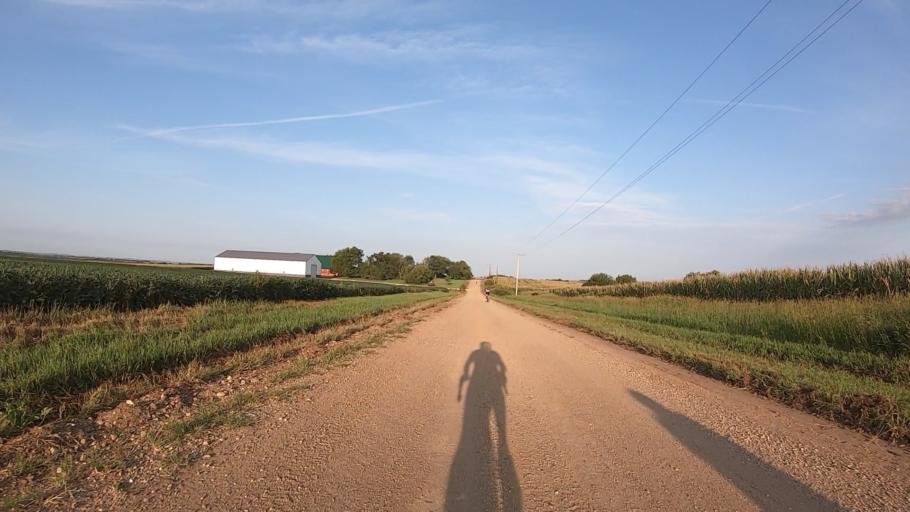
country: US
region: Kansas
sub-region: Marshall County
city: Marysville
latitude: 39.7694
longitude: -96.7451
